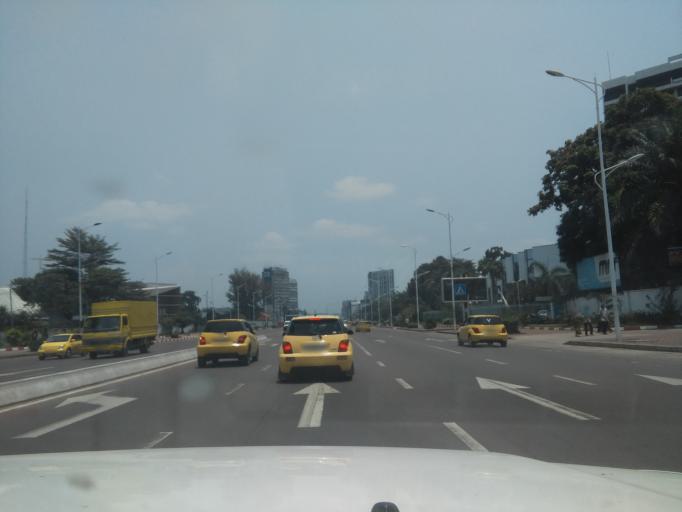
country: CD
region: Kinshasa
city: Kinshasa
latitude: -4.3090
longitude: 15.2913
